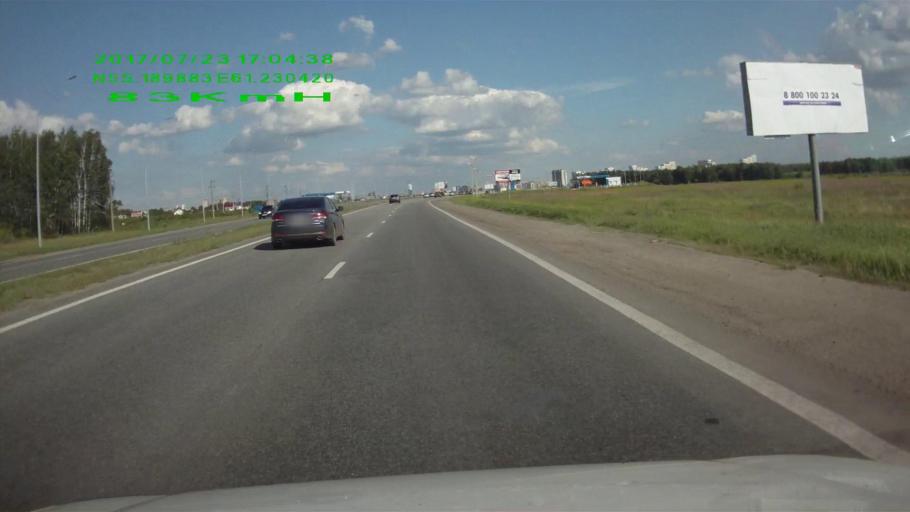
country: RU
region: Chelyabinsk
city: Roshchino
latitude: 55.1895
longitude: 61.2318
